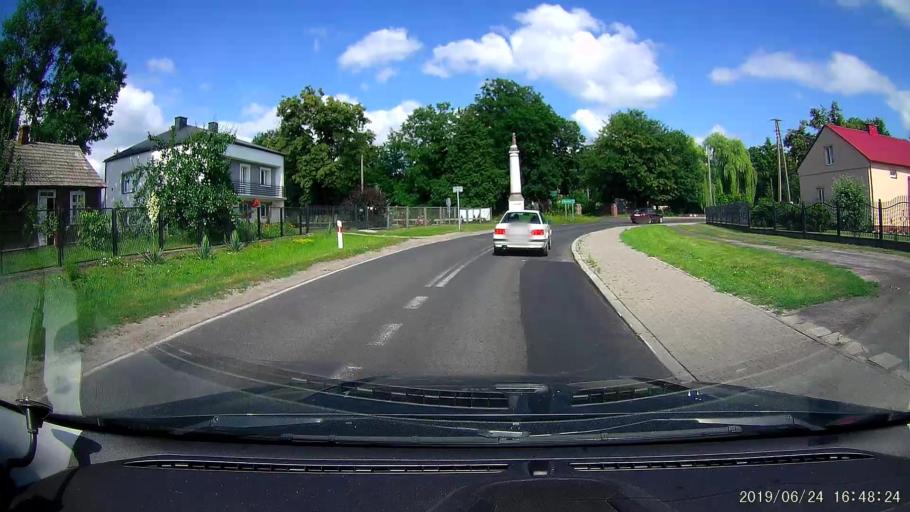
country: PL
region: Lublin Voivodeship
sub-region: Powiat tomaszowski
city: Laszczow
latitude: 50.5319
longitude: 23.7146
